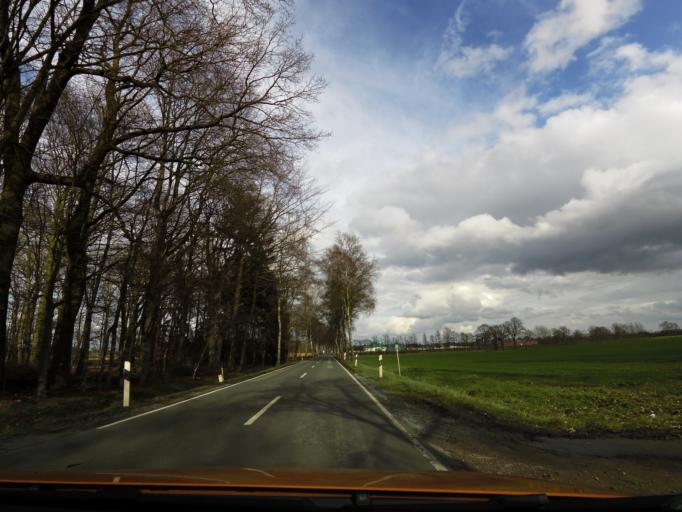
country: DE
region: Lower Saxony
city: Dunsen
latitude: 52.8881
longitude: 8.6411
